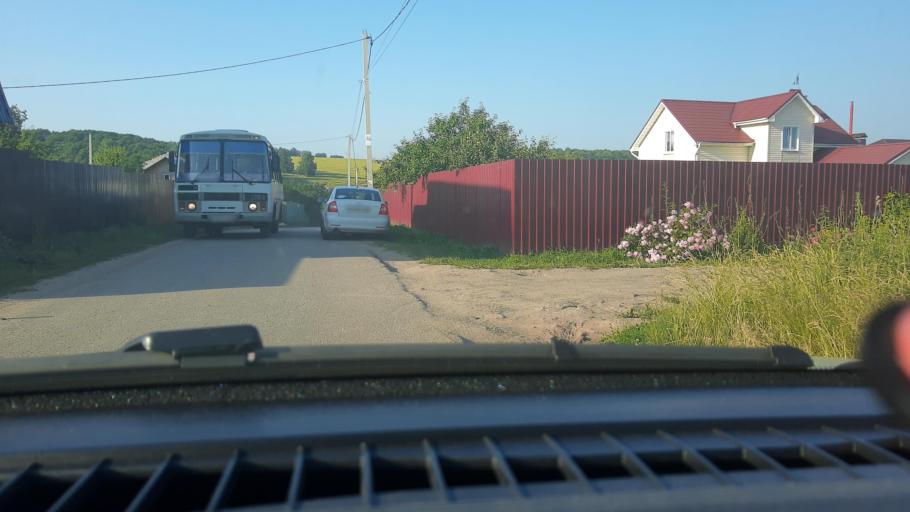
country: RU
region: Nizjnij Novgorod
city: Nizhniy Novgorod
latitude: 56.1960
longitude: 43.9578
